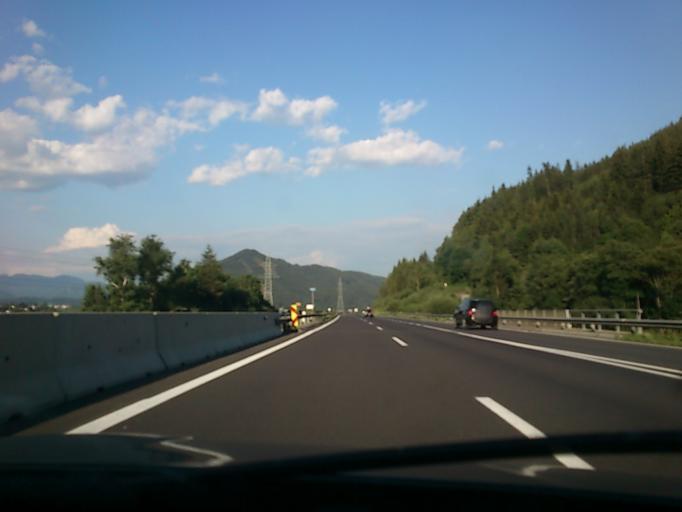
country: AT
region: Styria
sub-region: Politischer Bezirk Leoben
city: Kammern im Liesingtal
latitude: 47.3869
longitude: 14.9026
